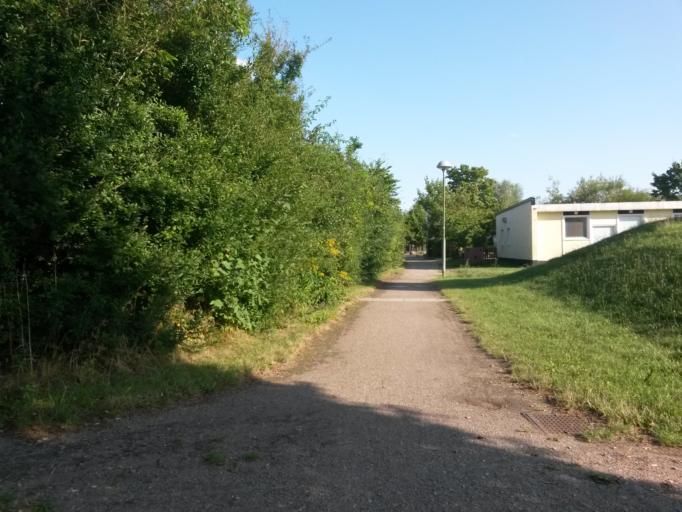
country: SE
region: Skane
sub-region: Lunds Kommun
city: Lund
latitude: 55.7050
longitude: 13.2355
